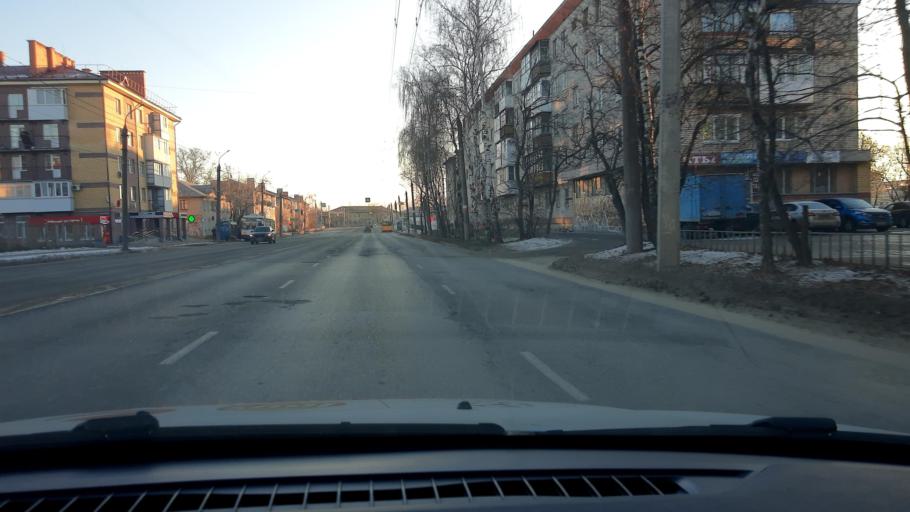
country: RU
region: Nizjnij Novgorod
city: Dzerzhinsk
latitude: 56.2477
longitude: 43.4700
